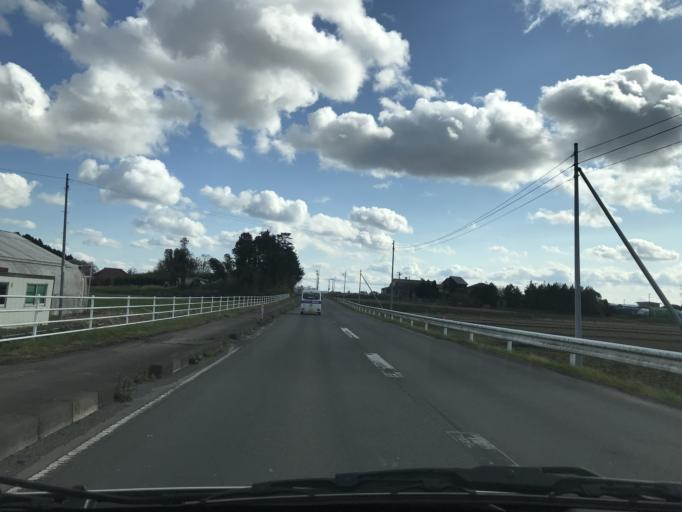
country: JP
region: Miyagi
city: Wakuya
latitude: 38.6551
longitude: 141.1924
